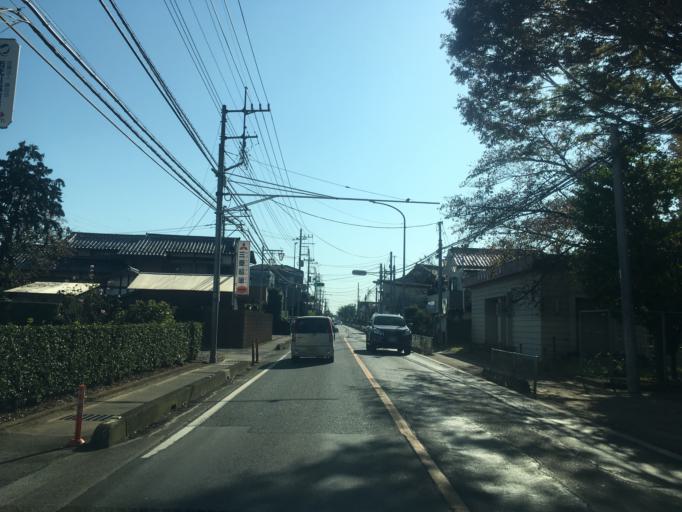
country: JP
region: Saitama
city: Kawagoe
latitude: 35.8724
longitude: 139.4734
